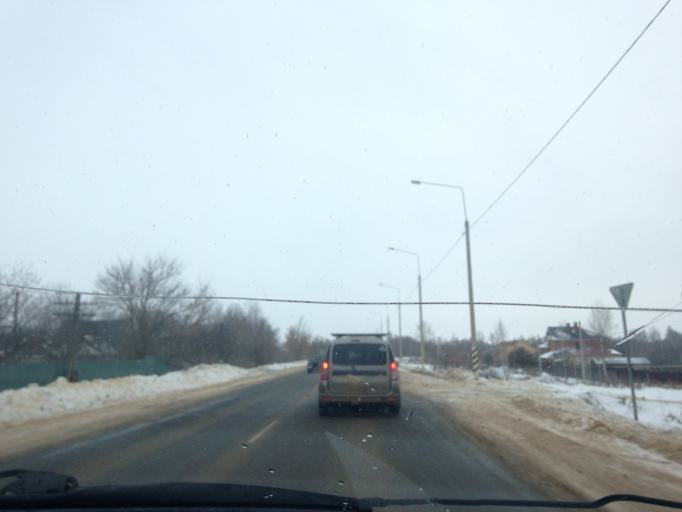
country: RU
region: Tula
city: Shchekino
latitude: 53.9858
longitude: 37.5041
